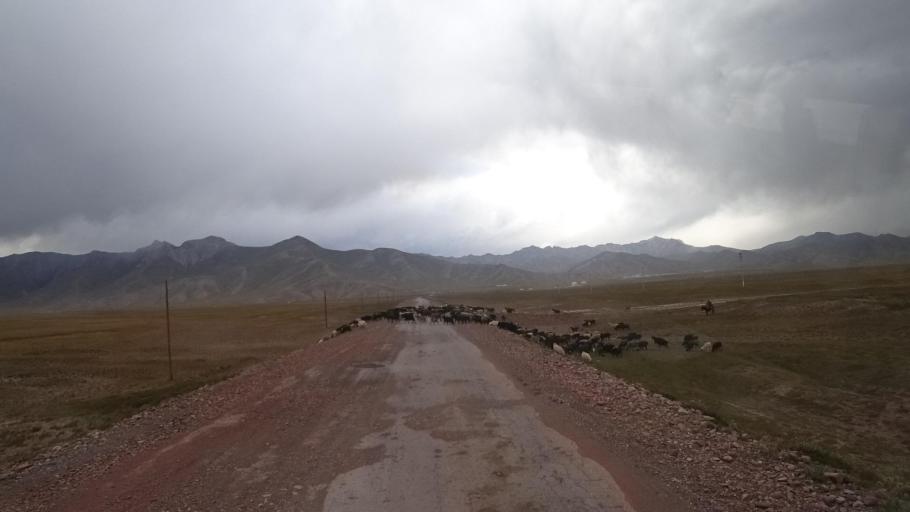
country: KG
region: Osh
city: Gul'cha
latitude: 39.6764
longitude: 73.2338
